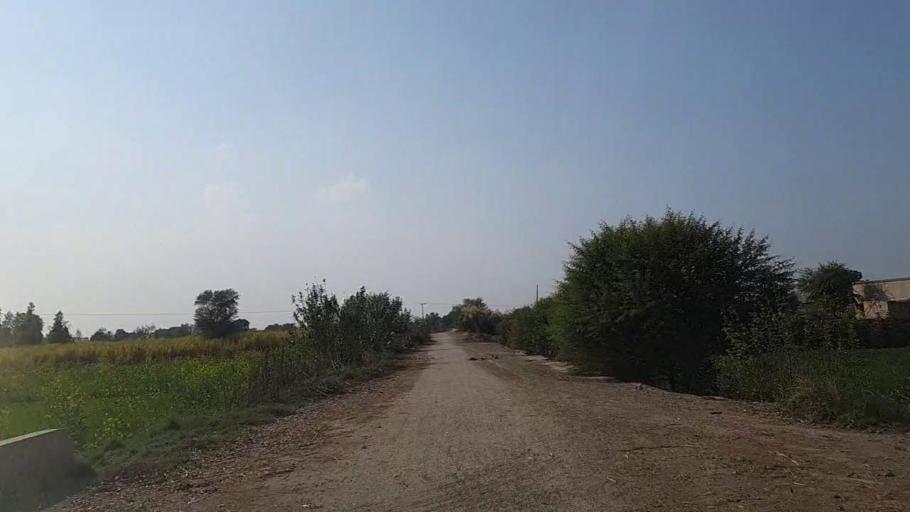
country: PK
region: Sindh
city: Jam Sahib
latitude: 26.2899
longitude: 68.5633
